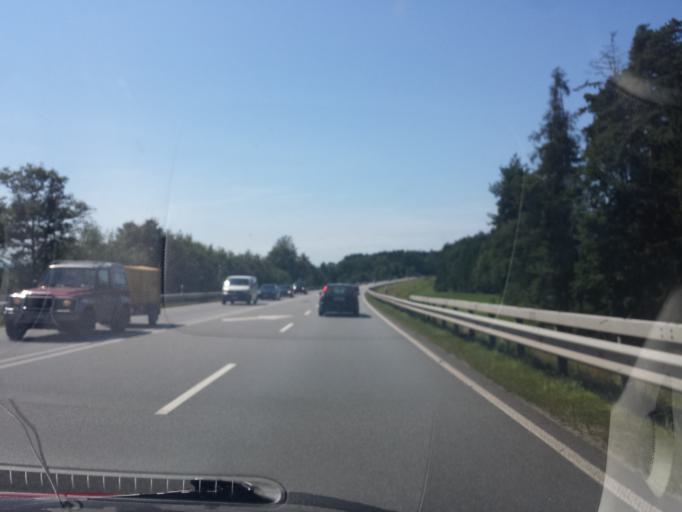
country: DE
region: Bavaria
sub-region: Upper Palatinate
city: Weiding
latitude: 49.2735
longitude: 12.7794
